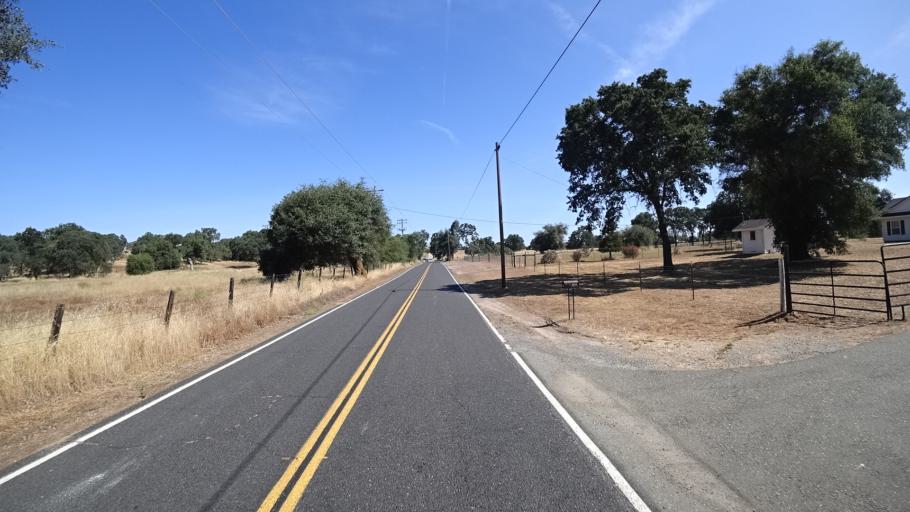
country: US
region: California
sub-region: Calaveras County
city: Rancho Calaveras
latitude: 38.1326
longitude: -120.9265
